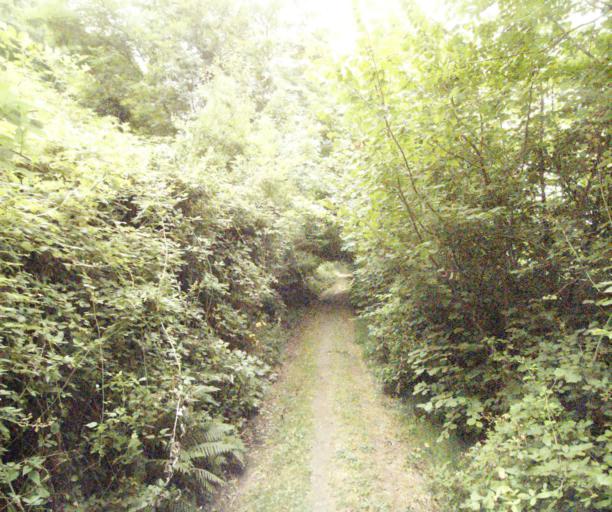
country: FR
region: Midi-Pyrenees
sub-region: Departement du Tarn
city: Soreze
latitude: 43.4394
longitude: 2.0632
